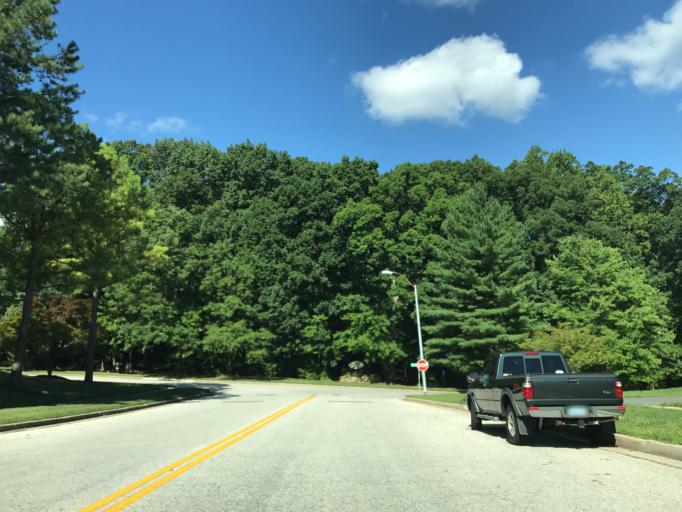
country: US
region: Maryland
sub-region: Baltimore County
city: Woodlawn
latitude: 39.3004
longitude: -76.7640
